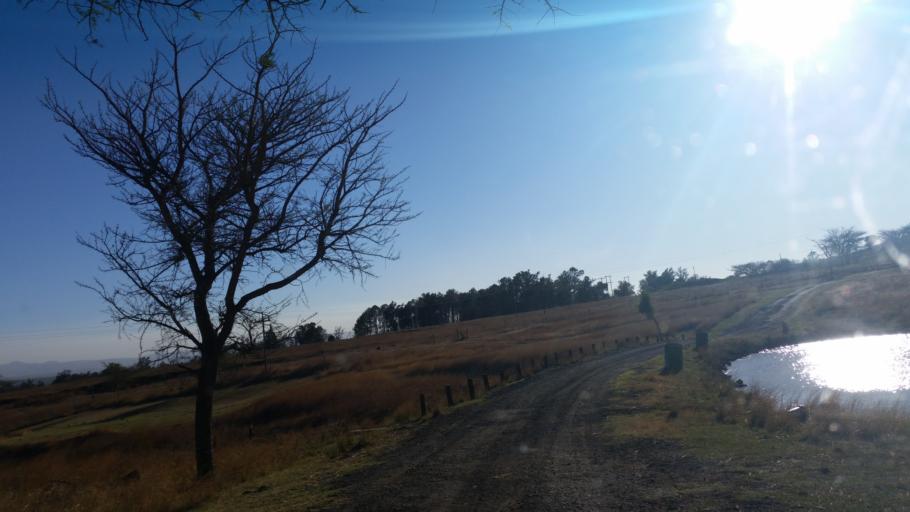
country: ZA
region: KwaZulu-Natal
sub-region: Amajuba District Municipality
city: Newcastle
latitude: -27.8026
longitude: 29.9537
